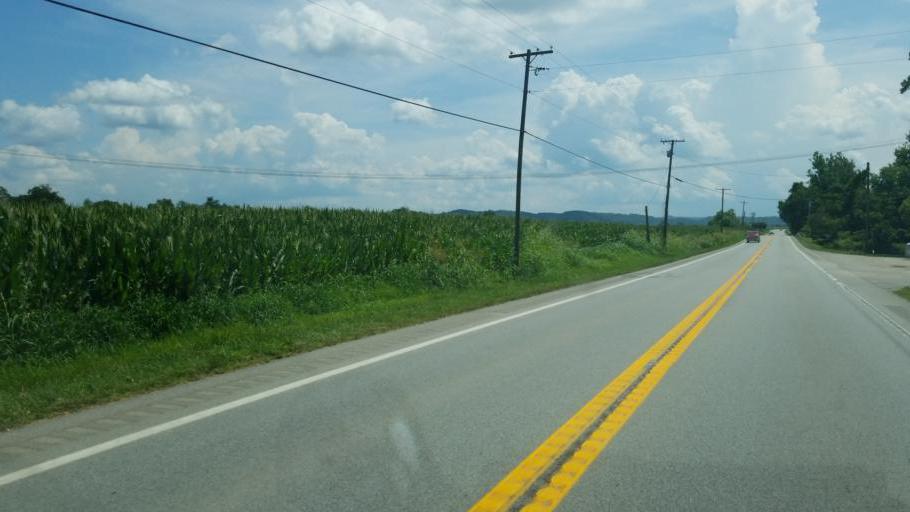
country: US
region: West Virginia
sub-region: Putnam County
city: Buffalo
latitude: 38.7452
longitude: -81.9811
